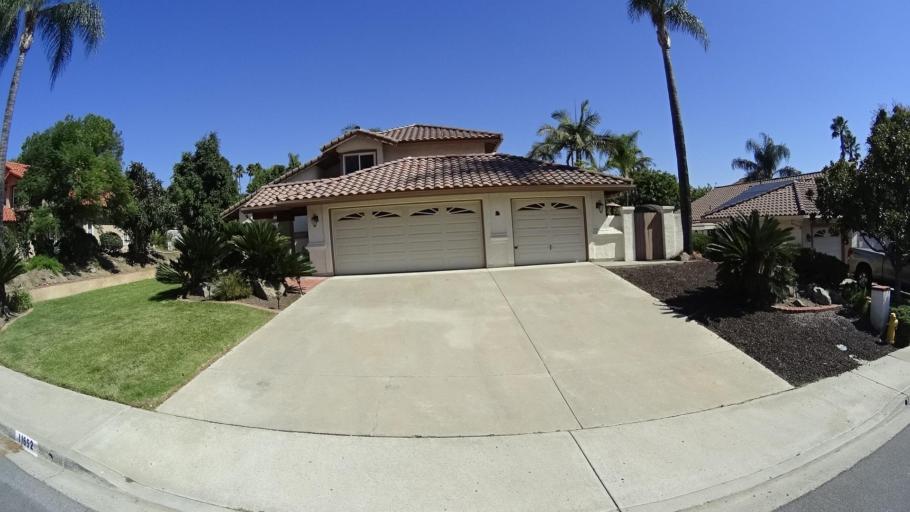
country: US
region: California
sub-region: San Diego County
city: Rancho San Diego
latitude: 32.7553
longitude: -116.9406
